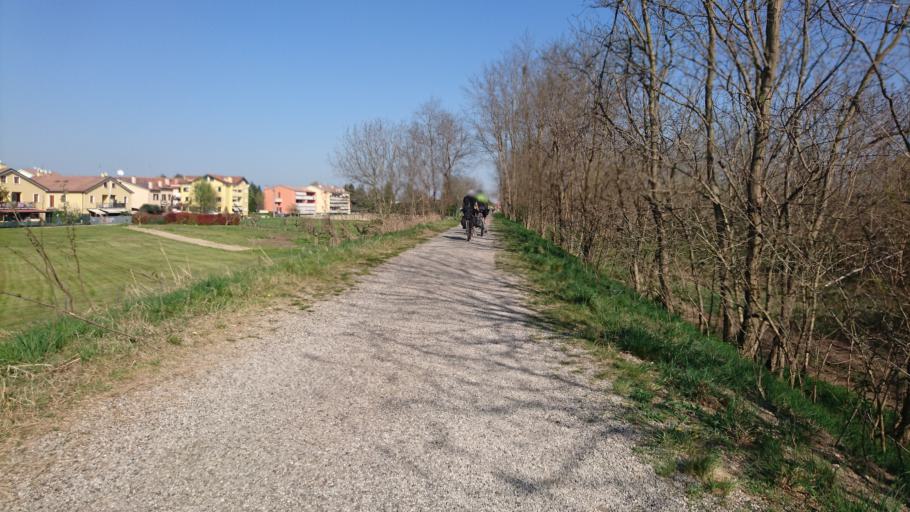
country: IT
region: Veneto
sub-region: Provincia di Padova
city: Saletto
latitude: 45.4715
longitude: 11.8564
